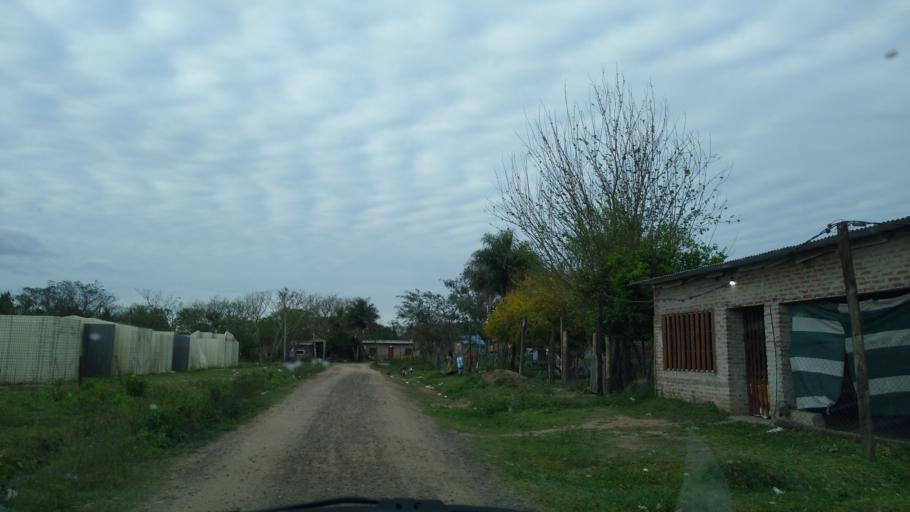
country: AR
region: Chaco
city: Fontana
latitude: -27.4019
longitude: -59.0381
